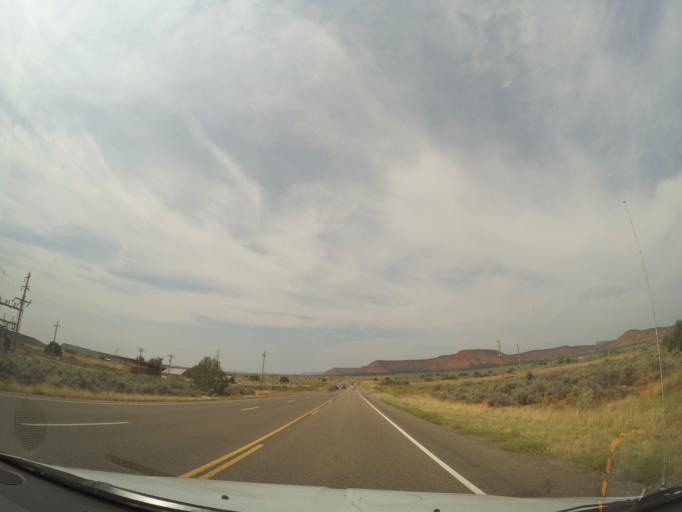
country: US
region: Utah
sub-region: Kane County
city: Kanab
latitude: 37.0377
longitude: -112.3523
